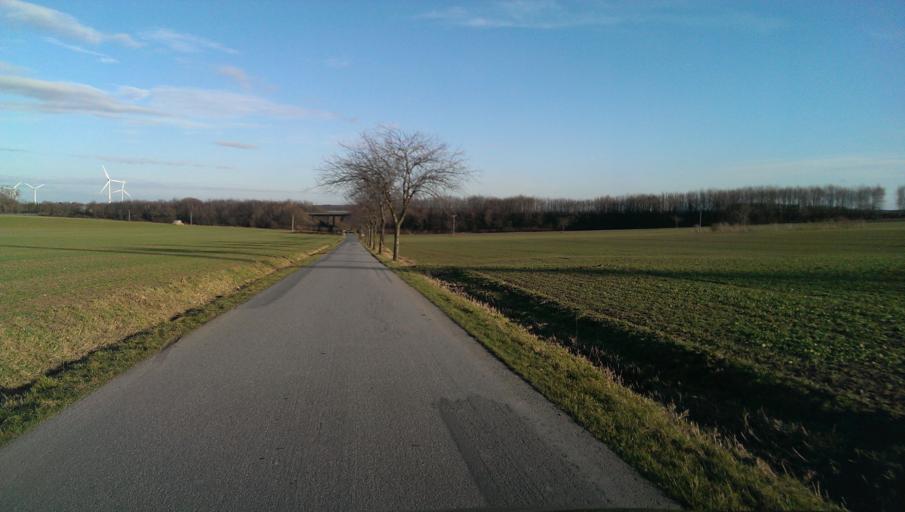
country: DE
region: North Rhine-Westphalia
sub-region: Regierungsbezirk Arnsberg
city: Ruthen
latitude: 51.5202
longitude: 8.4494
